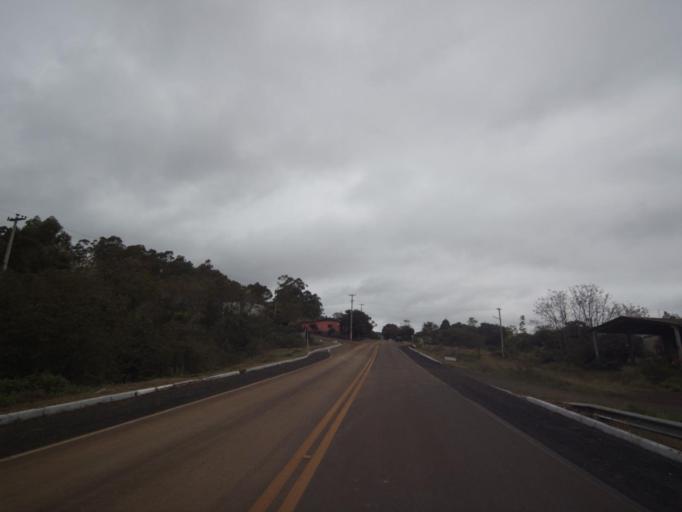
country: AR
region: Misiones
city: El Soberbio
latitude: -27.2943
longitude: -54.1901
